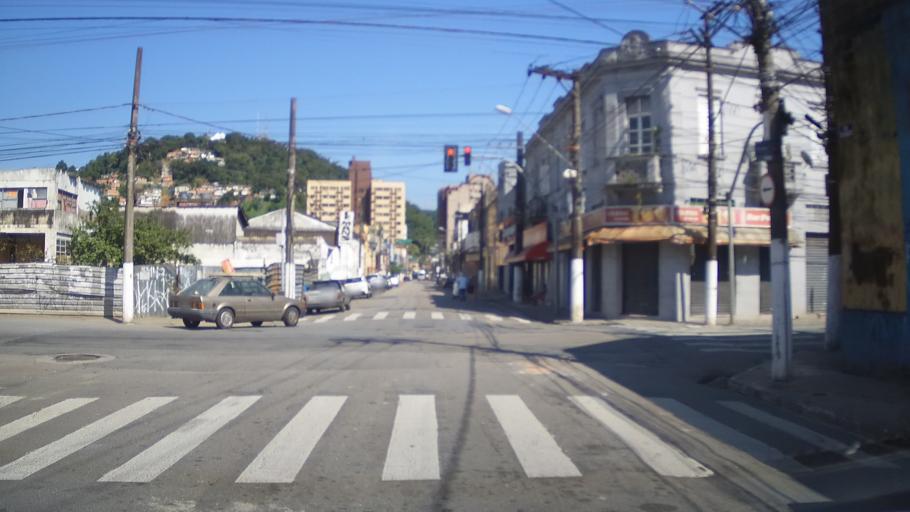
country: BR
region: Sao Paulo
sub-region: Santos
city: Santos
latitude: -23.9392
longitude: -46.3209
